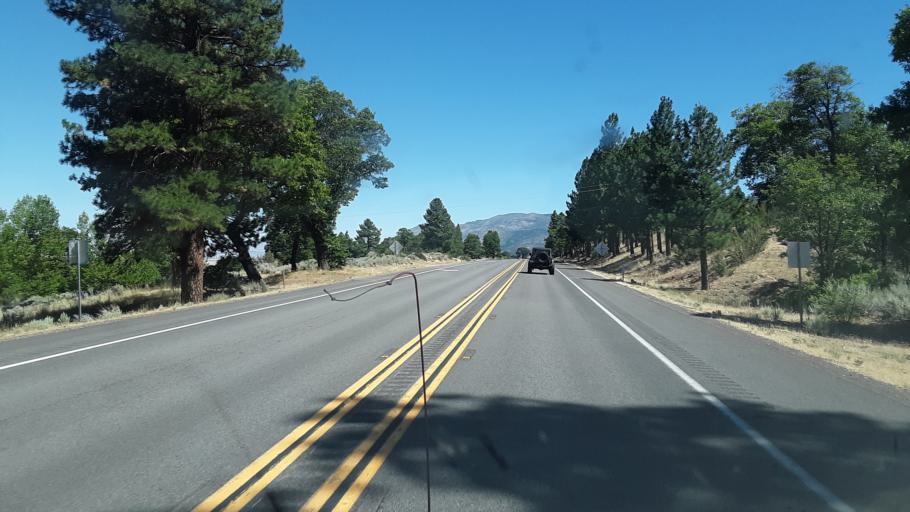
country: US
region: California
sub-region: Lassen County
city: Janesville
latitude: 40.2203
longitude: -120.4317
